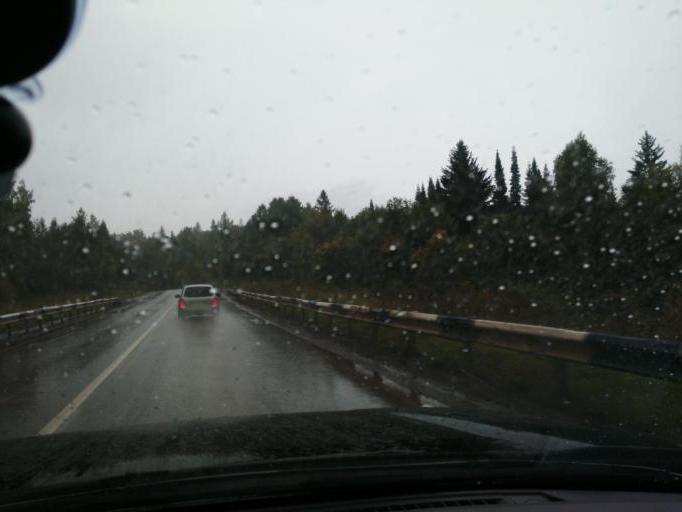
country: RU
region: Perm
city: Barda
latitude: 56.9020
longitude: 55.6977
